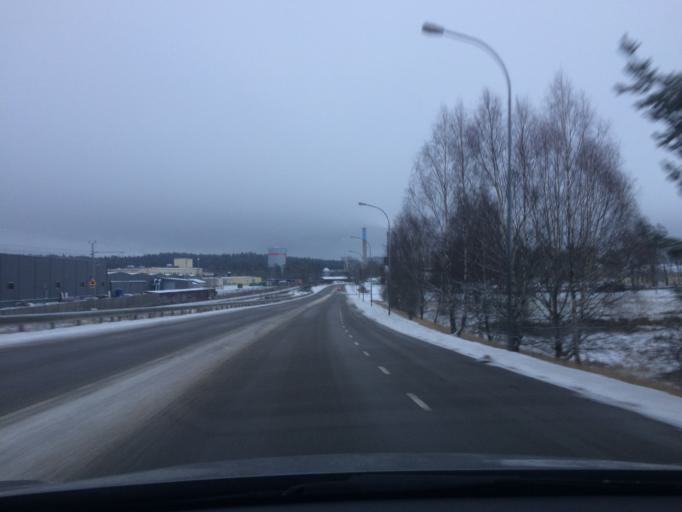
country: SE
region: Kronoberg
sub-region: Vaxjo Kommun
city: Vaexjoe
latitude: 56.8712
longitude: 14.8218
